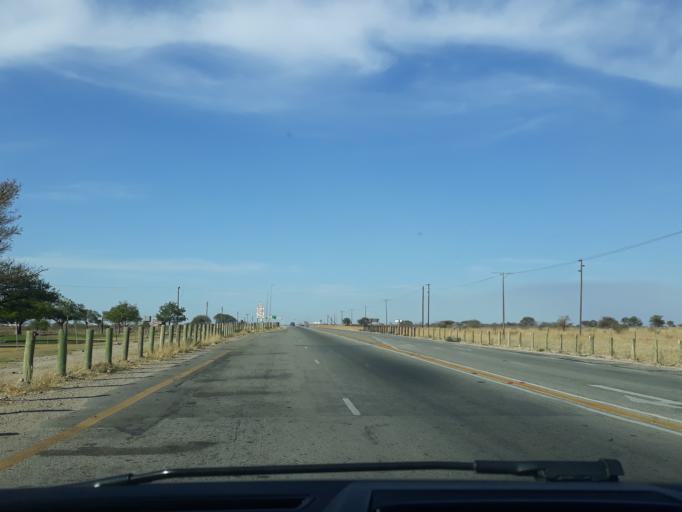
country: ZA
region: Limpopo
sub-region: Capricorn District Municipality
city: Polokwane
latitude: -23.9582
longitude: 29.3908
